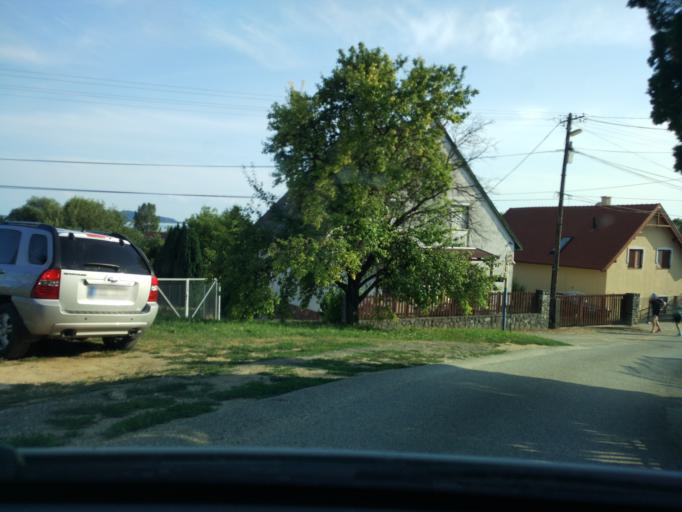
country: HU
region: Veszprem
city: Badacsonytomaj
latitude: 46.8065
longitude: 17.5431
